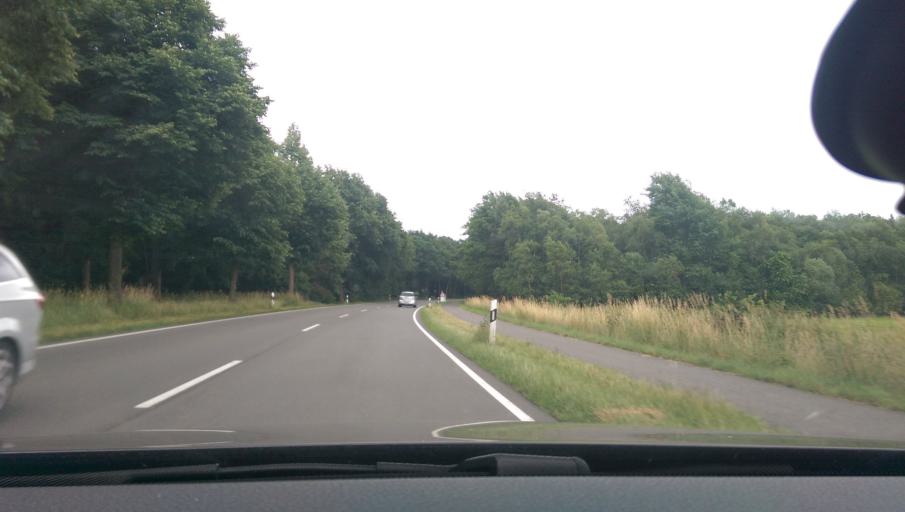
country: DE
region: Lower Saxony
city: Botersen
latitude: 53.1639
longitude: 9.3183
